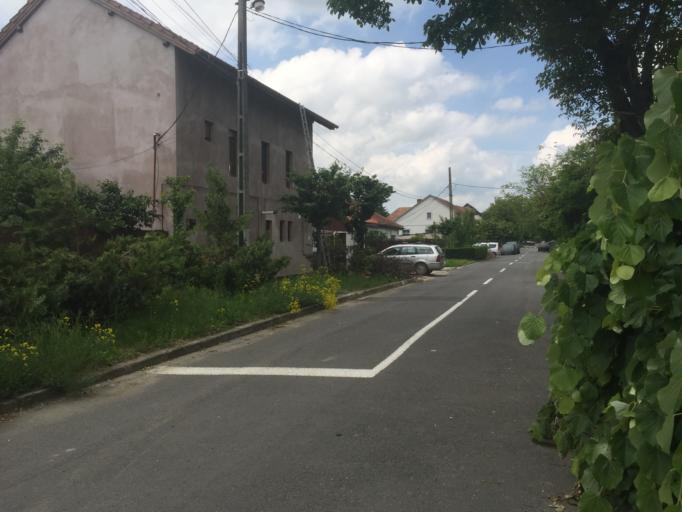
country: RO
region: Timis
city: Timisoara
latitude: 45.7566
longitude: 21.2045
